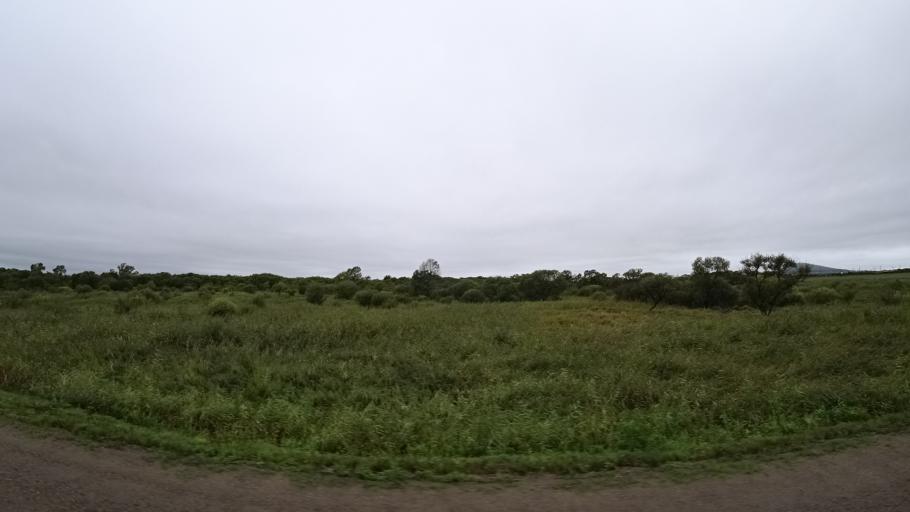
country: RU
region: Primorskiy
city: Monastyrishche
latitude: 44.2204
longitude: 132.4518
